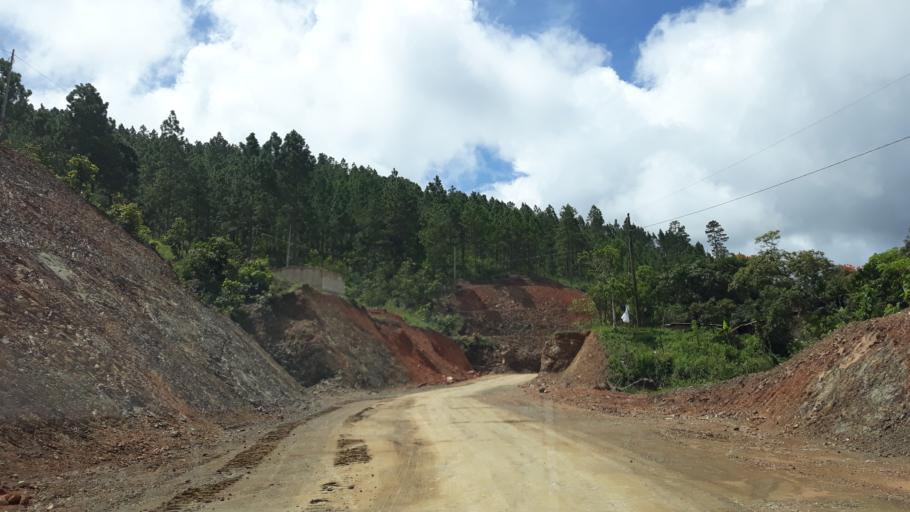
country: HN
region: El Paraiso
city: Santa Cruz
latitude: 13.7638
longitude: -86.6467
